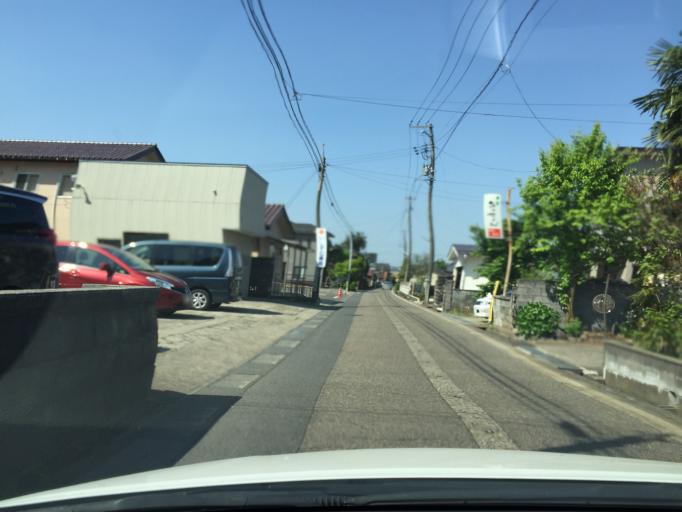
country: JP
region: Niigata
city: Muramatsu
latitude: 37.6970
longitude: 139.1838
